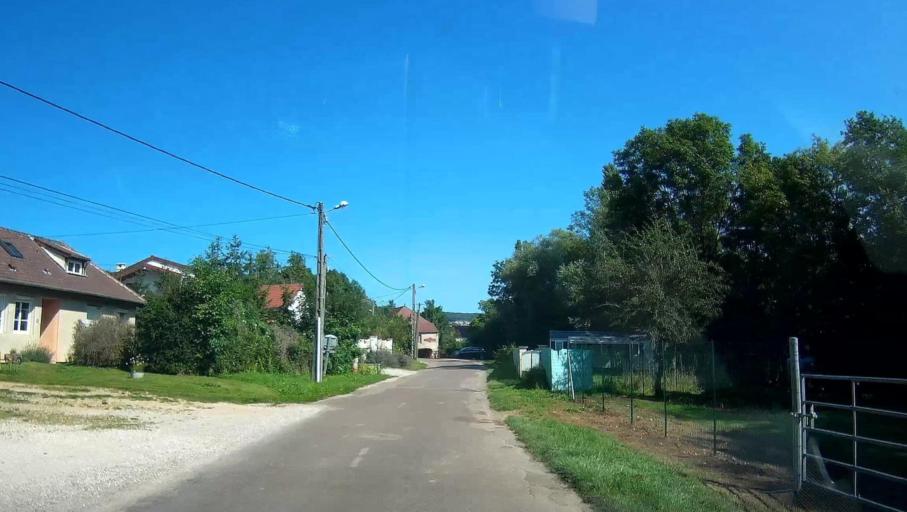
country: FR
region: Bourgogne
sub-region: Departement de la Cote-d'Or
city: Nolay
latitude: 46.9652
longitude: 4.6431
